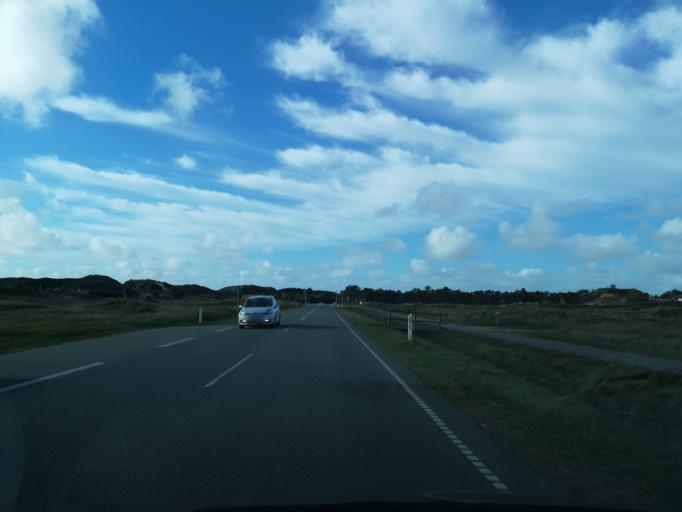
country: DK
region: South Denmark
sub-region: Varde Kommune
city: Oksbol
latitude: 55.7344
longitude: 8.1915
